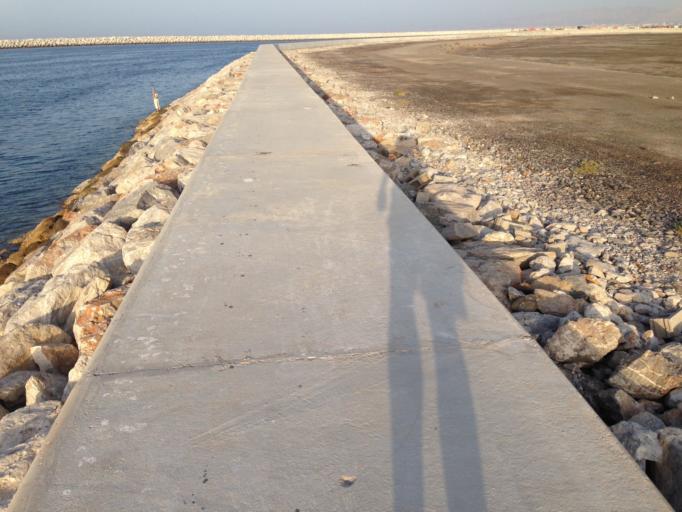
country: OM
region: Muhafazat Masqat
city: As Sib al Jadidah
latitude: 23.6350
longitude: 58.2669
